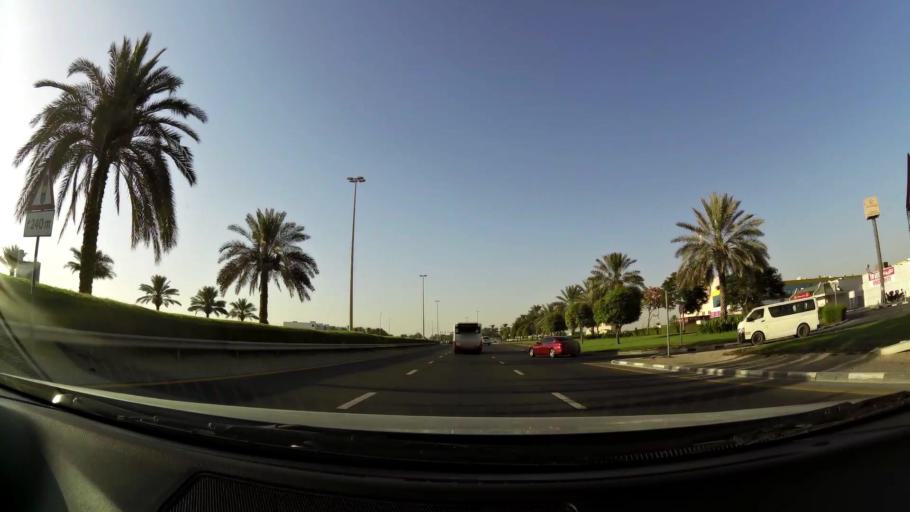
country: AE
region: Ash Shariqah
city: Sharjah
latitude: 25.2015
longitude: 55.3757
